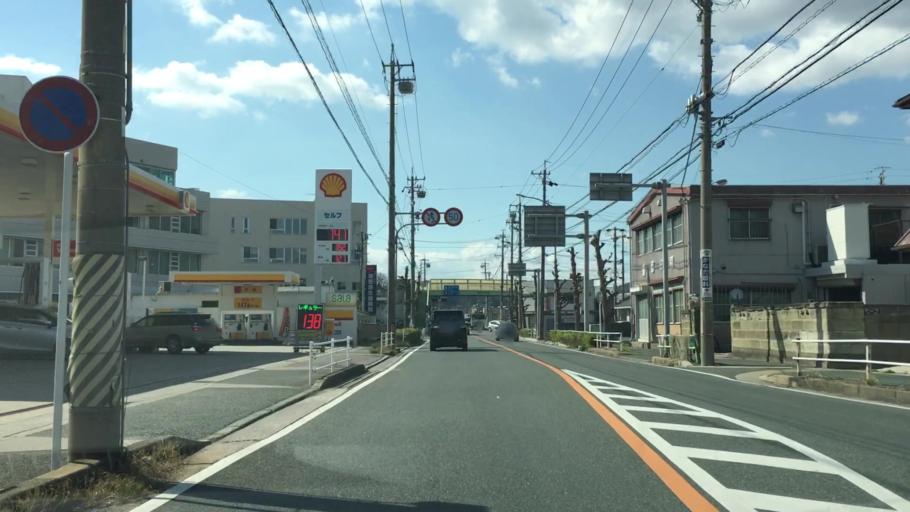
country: JP
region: Aichi
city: Gamagori
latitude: 34.8240
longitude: 137.2178
